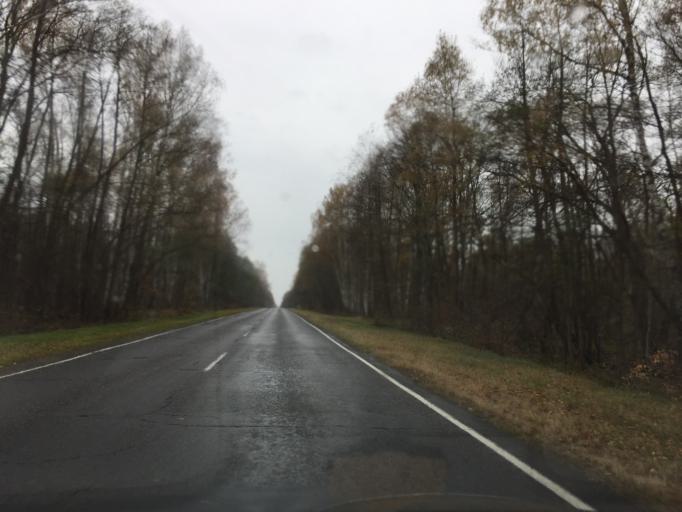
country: BY
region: Mogilev
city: Slawharad
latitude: 53.3723
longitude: 30.8653
